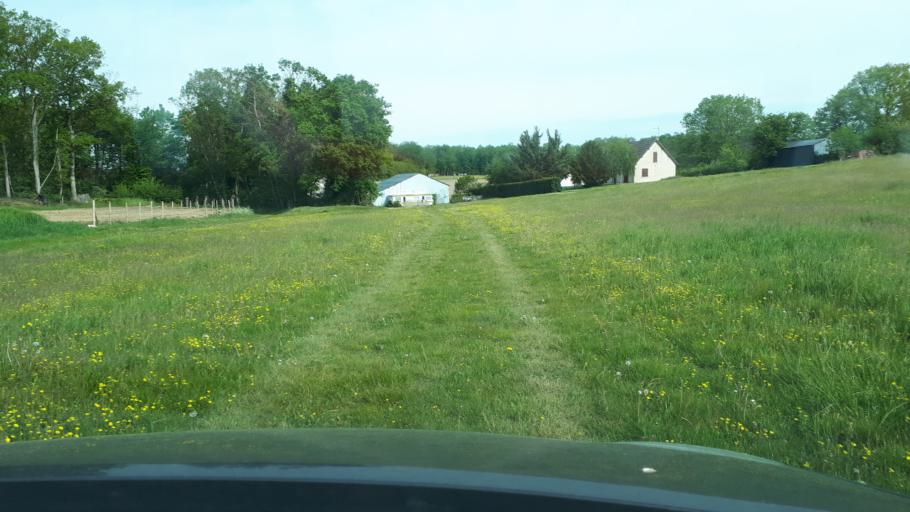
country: FR
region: Centre
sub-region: Departement du Loir-et-Cher
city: Naveil
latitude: 47.7699
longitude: 1.0169
